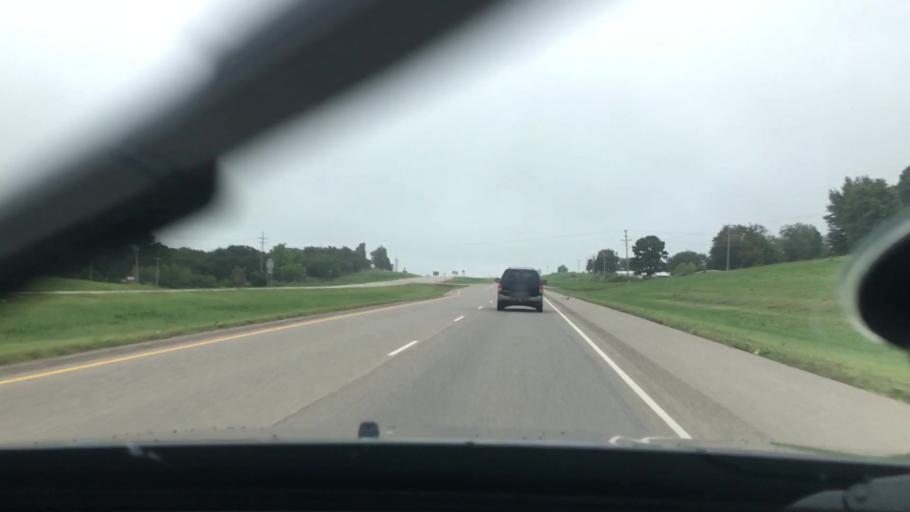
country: US
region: Oklahoma
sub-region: Seminole County
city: Seminole
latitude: 35.3025
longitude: -96.6707
